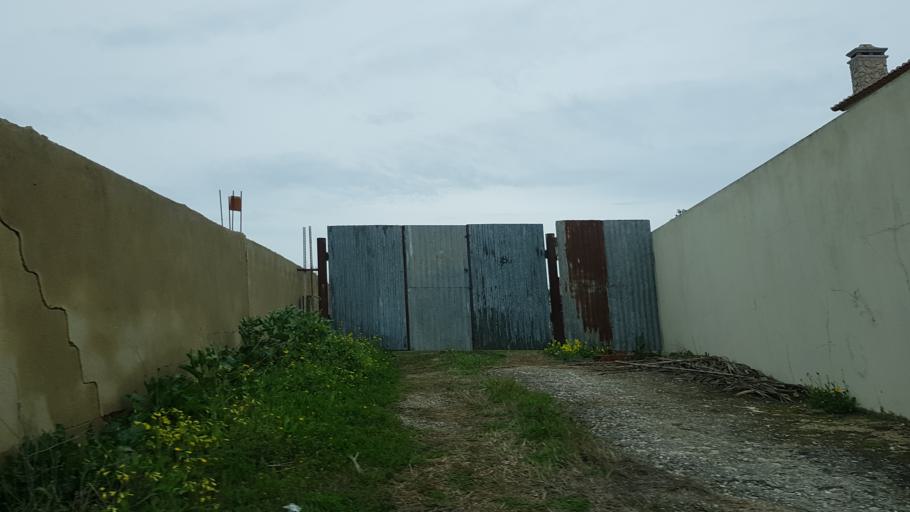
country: PT
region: Lisbon
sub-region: Alenquer
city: Carregado
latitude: 39.0399
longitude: -8.9773
